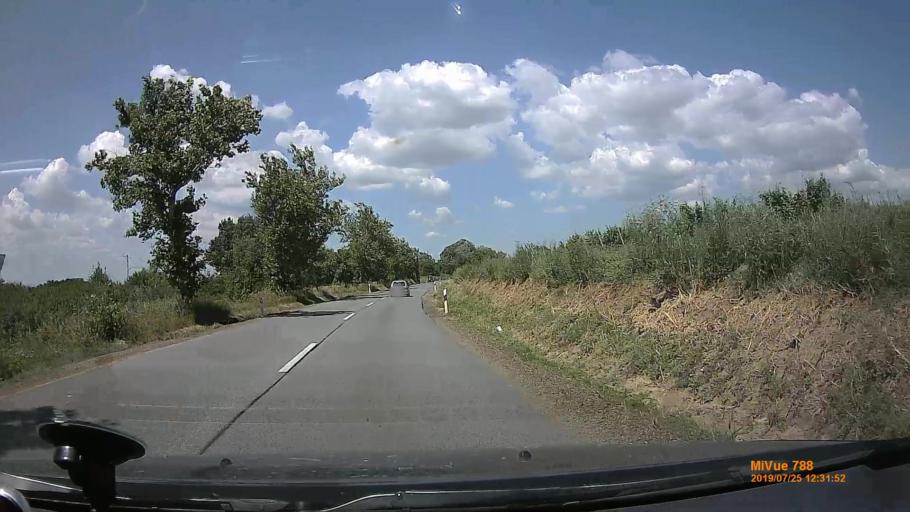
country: HU
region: Borsod-Abauj-Zemplen
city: Tarcal
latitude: 48.1459
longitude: 21.3223
